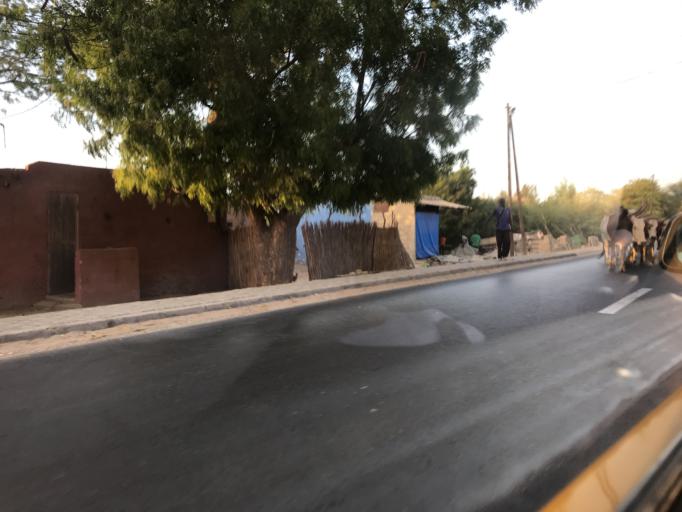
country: SN
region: Saint-Louis
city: Saint-Louis
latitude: 16.0379
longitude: -16.4608
